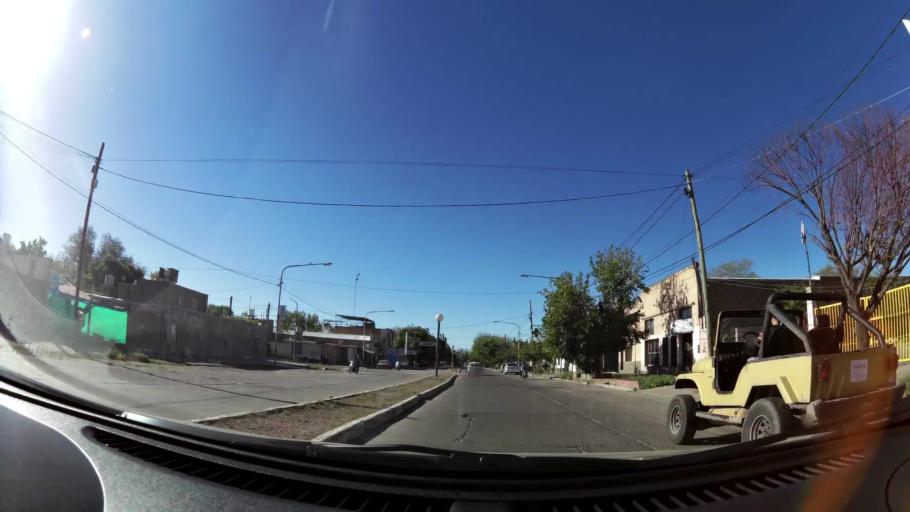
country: AR
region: Mendoza
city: Las Heras
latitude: -32.8618
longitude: -68.8217
